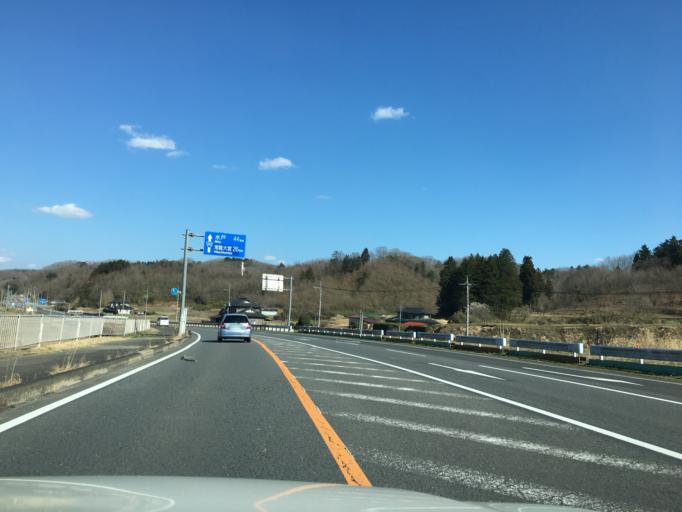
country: JP
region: Tochigi
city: Motegi
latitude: 36.5245
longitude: 140.1894
